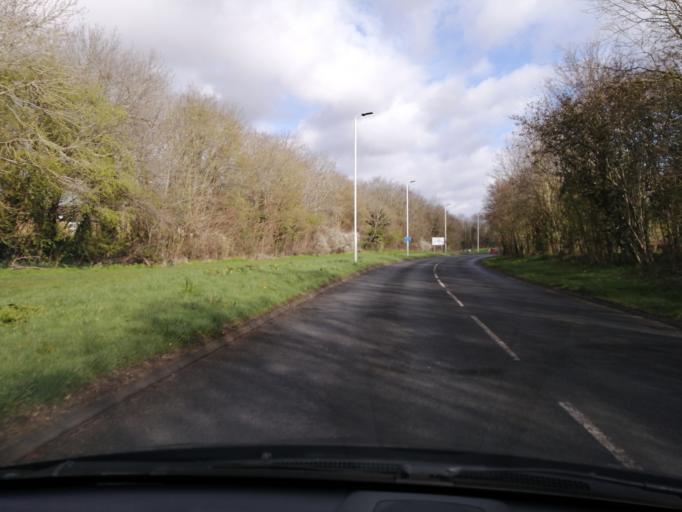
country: GB
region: England
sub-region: Peterborough
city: Marholm
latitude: 52.6016
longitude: -0.2887
